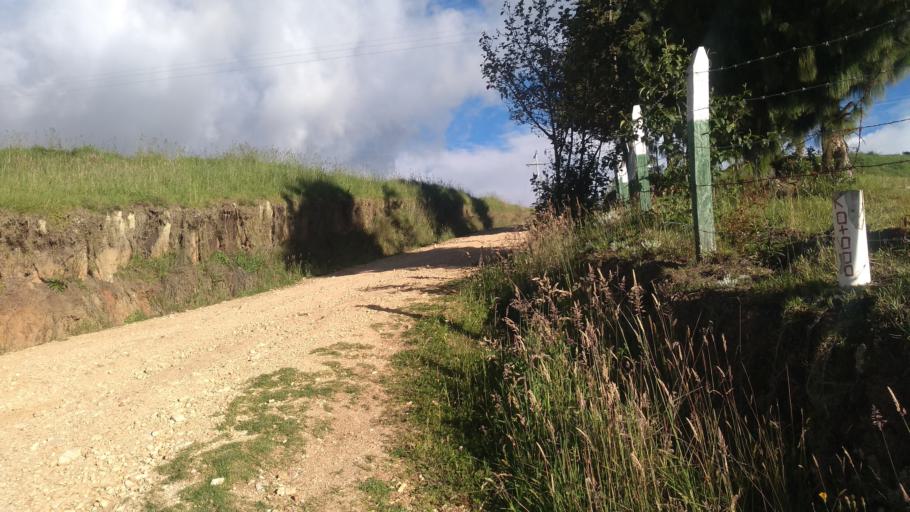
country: CO
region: Boyaca
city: Toca
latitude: 5.5604
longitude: -73.1689
